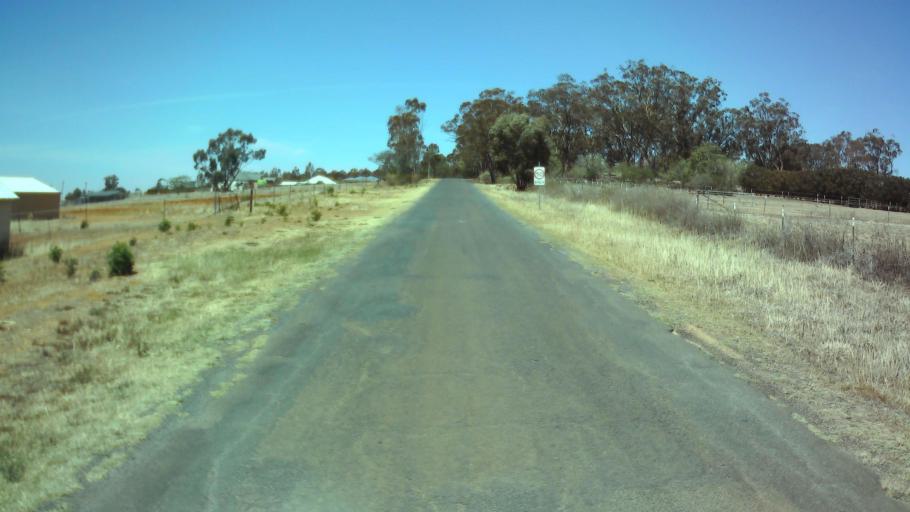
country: AU
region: New South Wales
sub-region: Weddin
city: Grenfell
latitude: -33.9009
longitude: 148.1732
